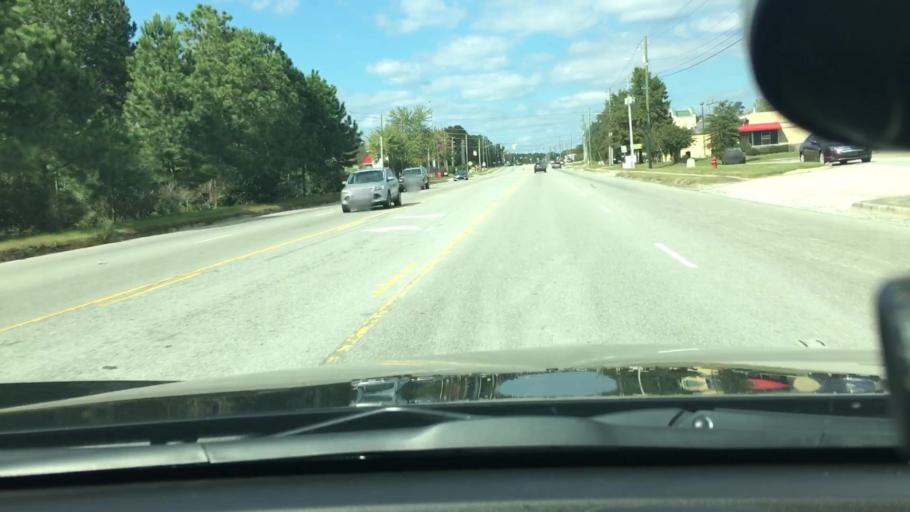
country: US
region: North Carolina
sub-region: Wake County
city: Apex
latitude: 35.7103
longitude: -78.8380
